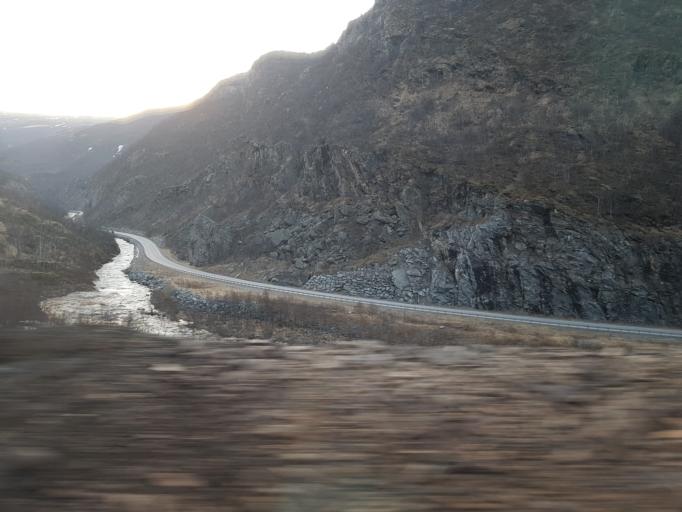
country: NO
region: Sor-Trondelag
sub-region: Oppdal
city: Oppdal
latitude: 62.3422
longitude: 9.6163
